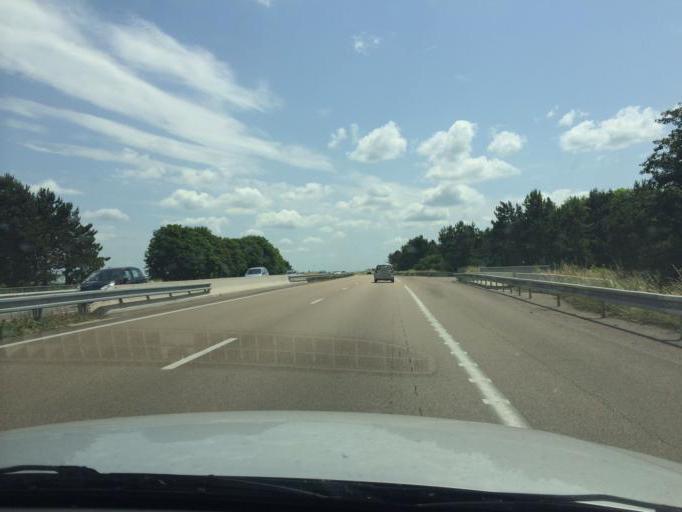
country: FR
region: Champagne-Ardenne
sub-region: Departement de la Marne
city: Verzy
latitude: 49.0974
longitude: 4.2556
